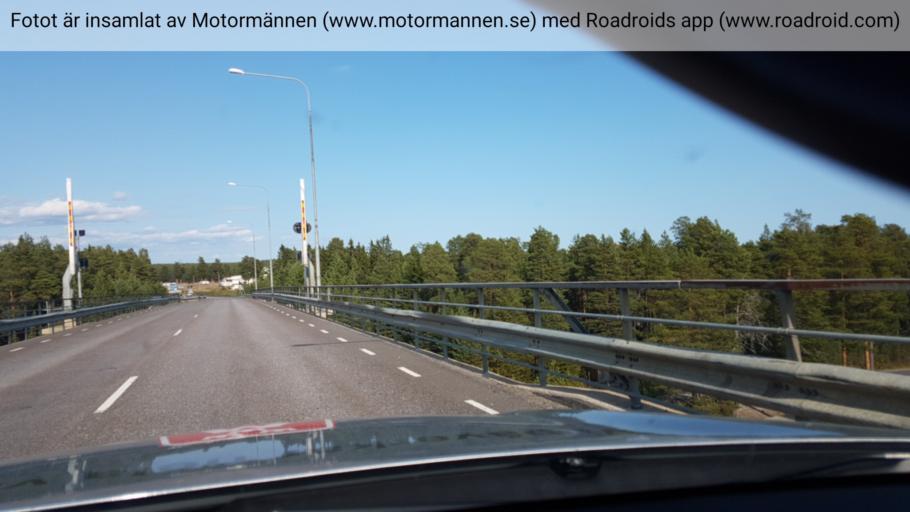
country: SE
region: Norrbotten
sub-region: Pitea Kommun
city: Pitea
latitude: 65.2318
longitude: 21.5174
